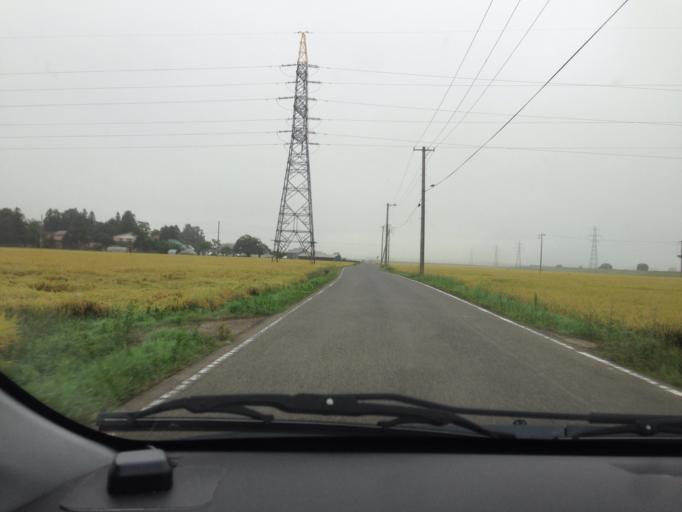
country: JP
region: Fukushima
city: Kitakata
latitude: 37.5759
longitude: 139.8661
